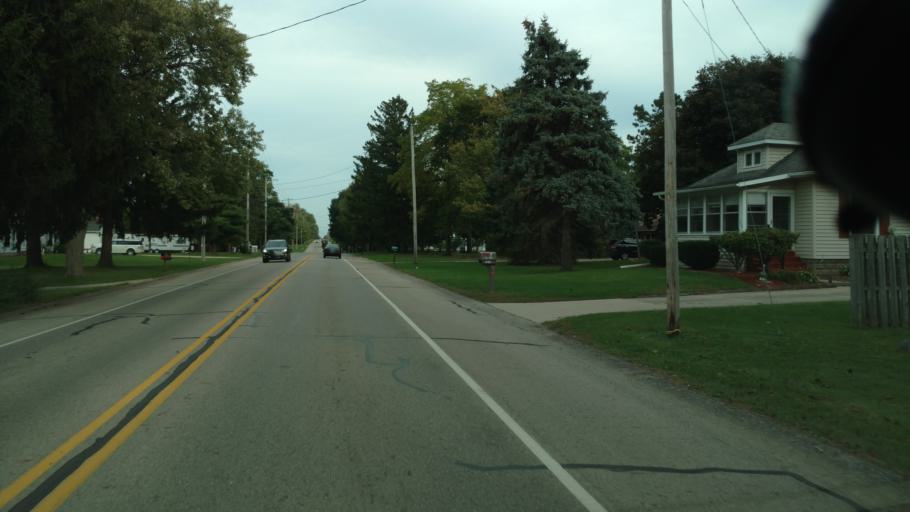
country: US
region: Michigan
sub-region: Ingham County
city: Lansing
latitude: 42.7842
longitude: -84.5389
